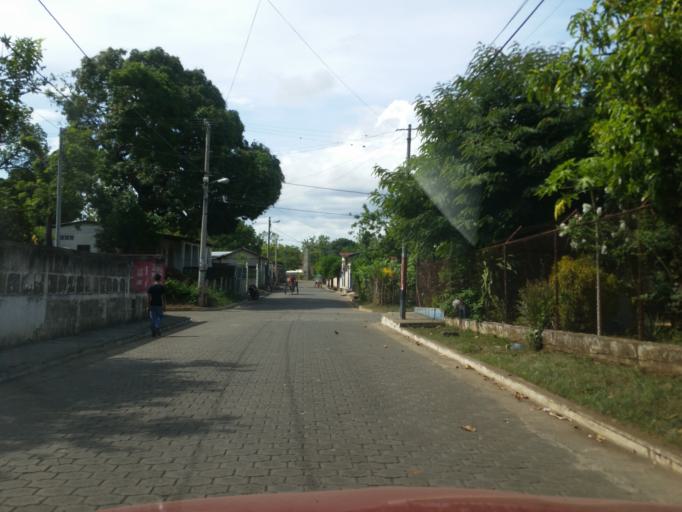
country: NI
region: Masaya
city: Nindiri
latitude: 12.0007
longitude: -86.1199
